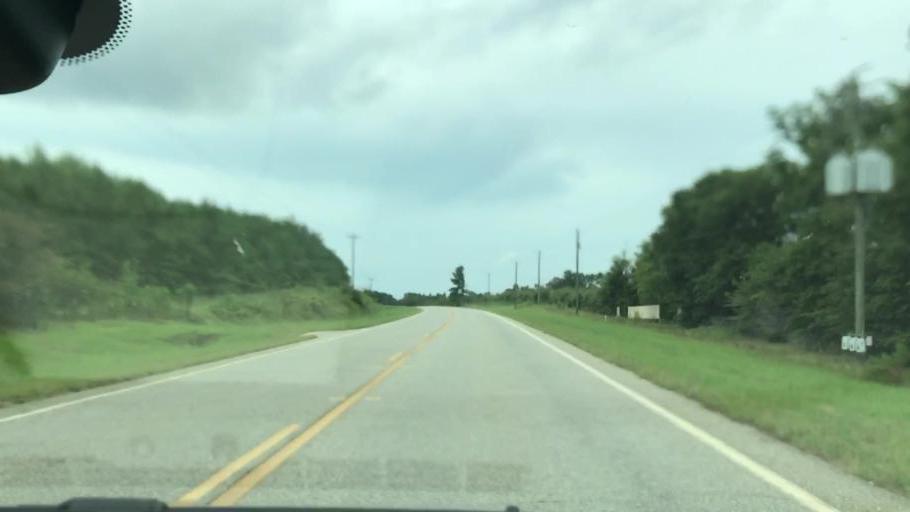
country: US
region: Georgia
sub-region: Clay County
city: Fort Gaines
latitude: 31.6771
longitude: -85.0471
